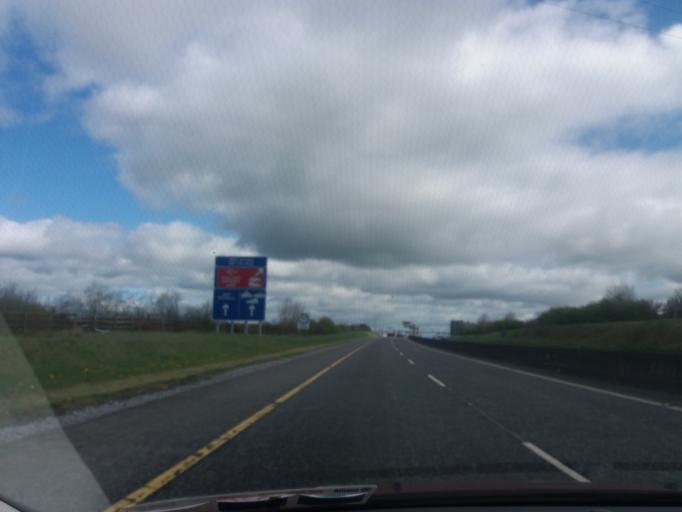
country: IE
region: Munster
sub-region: County Cork
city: Watergrasshill
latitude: 52.0229
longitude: -8.3323
